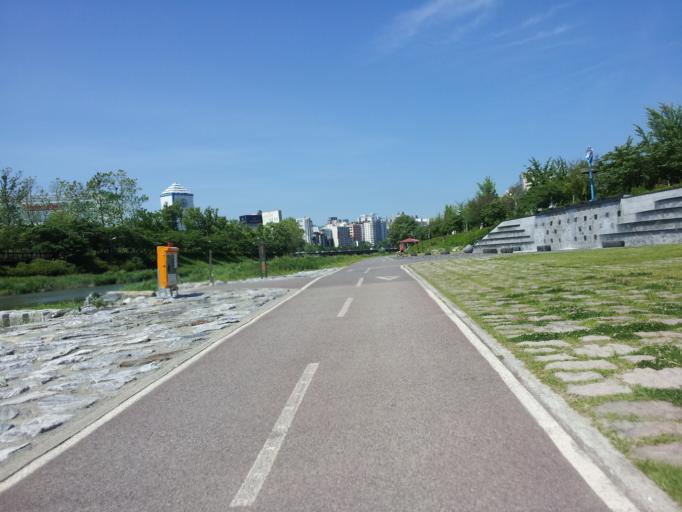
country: KR
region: Daejeon
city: Daejeon
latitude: 36.3615
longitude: 127.3577
